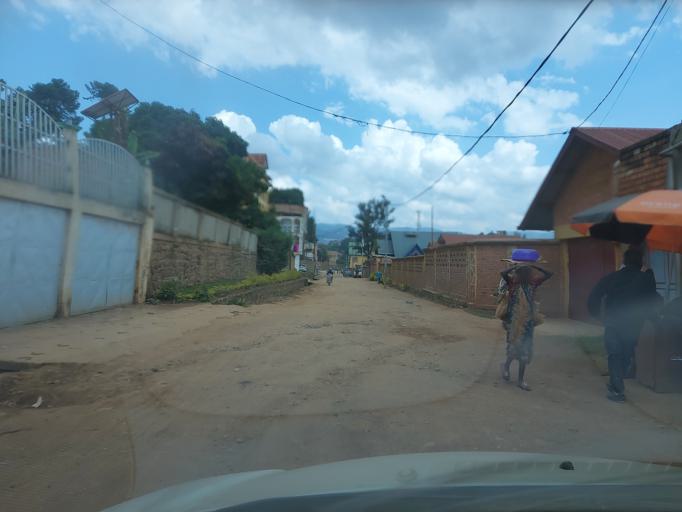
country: RW
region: Western Province
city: Cyangugu
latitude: -2.4983
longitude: 28.8833
